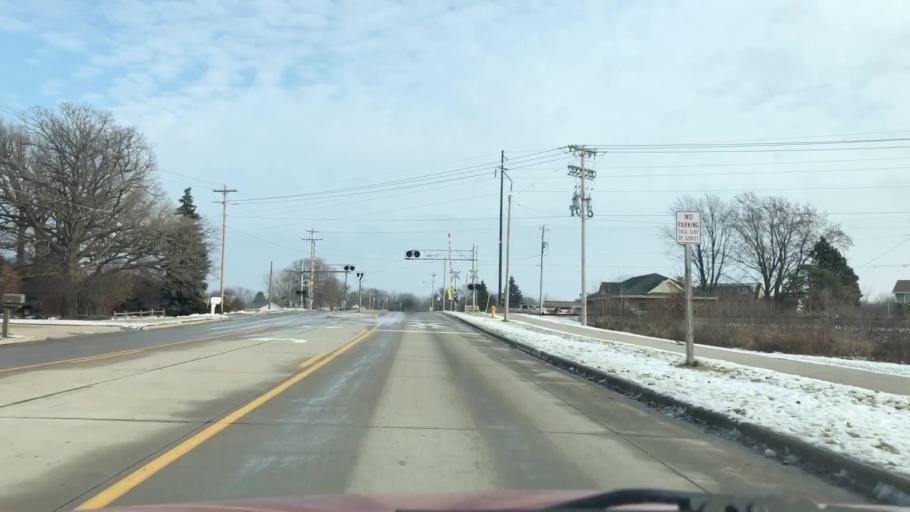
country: US
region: Wisconsin
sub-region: Brown County
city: De Pere
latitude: 44.4305
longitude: -88.0845
